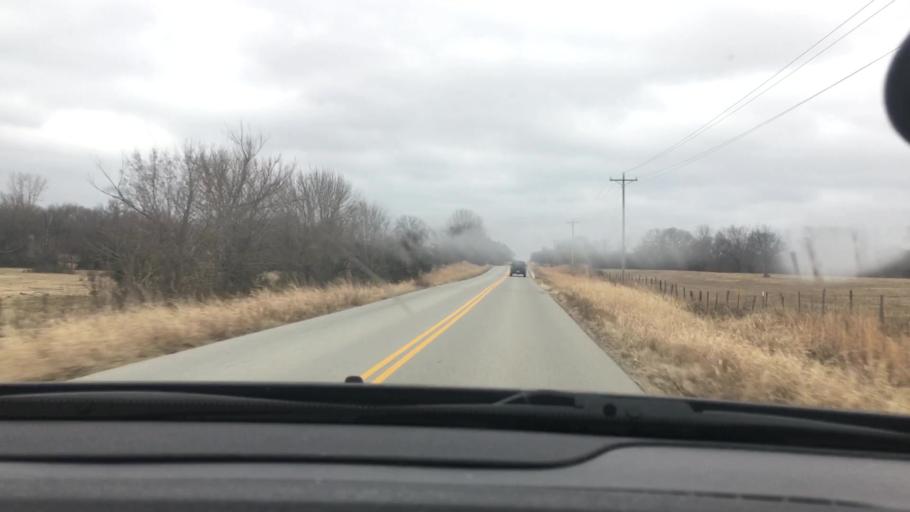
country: US
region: Oklahoma
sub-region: Atoka County
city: Atoka
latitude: 34.3222
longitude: -96.0755
